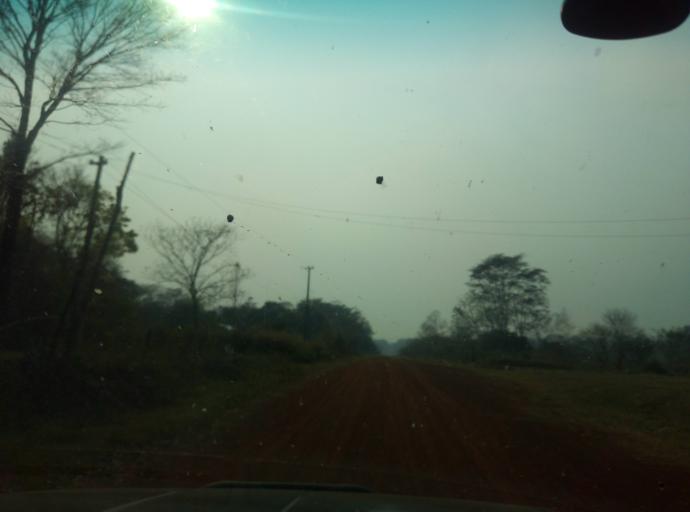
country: PY
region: Caaguazu
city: Carayao
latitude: -25.2039
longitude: -56.2396
